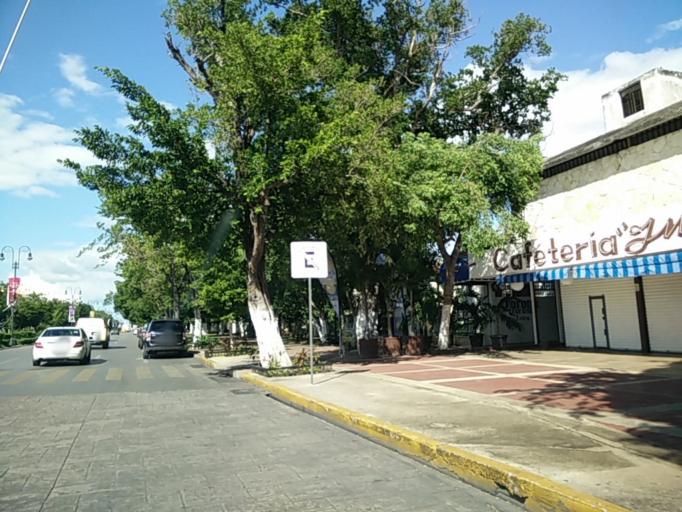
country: MX
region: Yucatan
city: Merida
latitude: 20.9753
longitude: -89.6195
